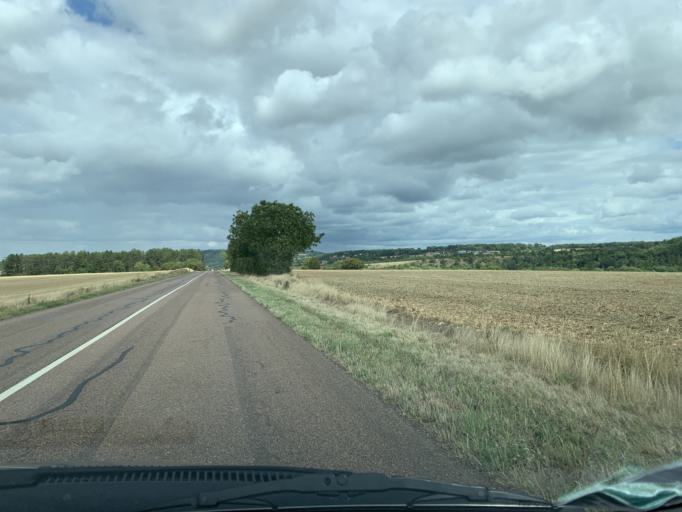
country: FR
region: Bourgogne
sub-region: Departement de la Nievre
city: Clamecy
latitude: 47.4421
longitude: 3.4942
